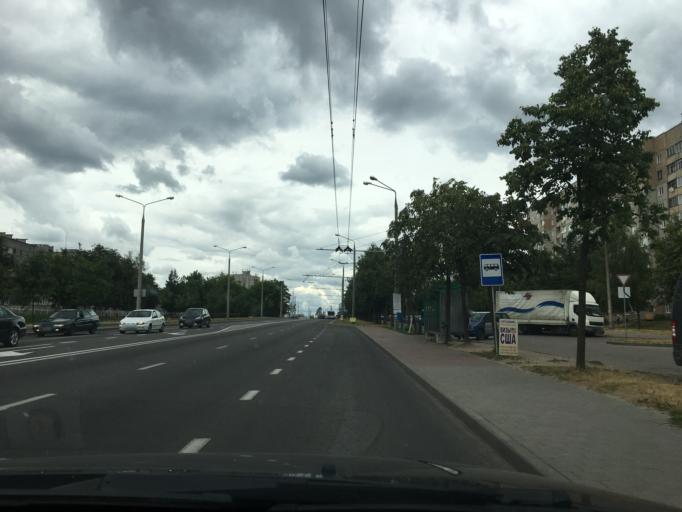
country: BY
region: Grodnenskaya
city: Hrodna
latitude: 53.6447
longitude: 23.8396
